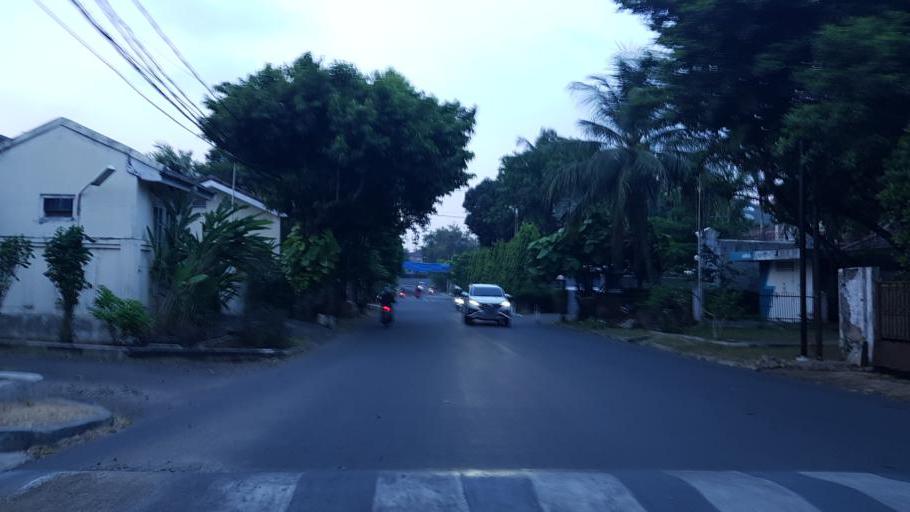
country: ID
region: West Java
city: Pamulang
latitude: -6.3183
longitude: 106.7849
